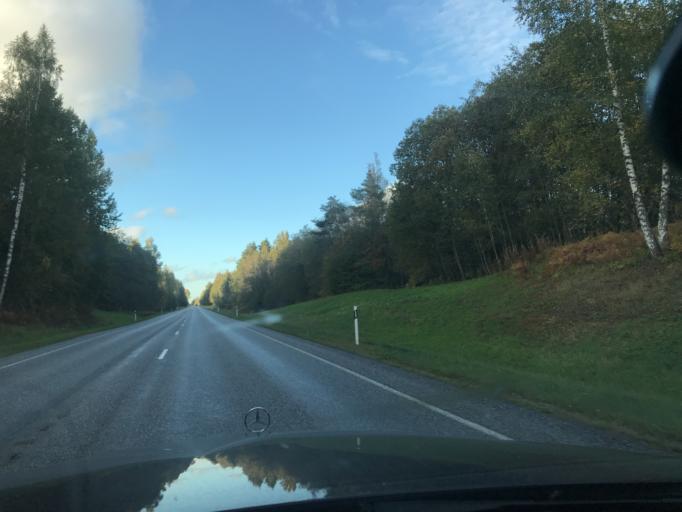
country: RU
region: Pskov
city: Pechory
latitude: 57.6611
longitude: 27.3311
